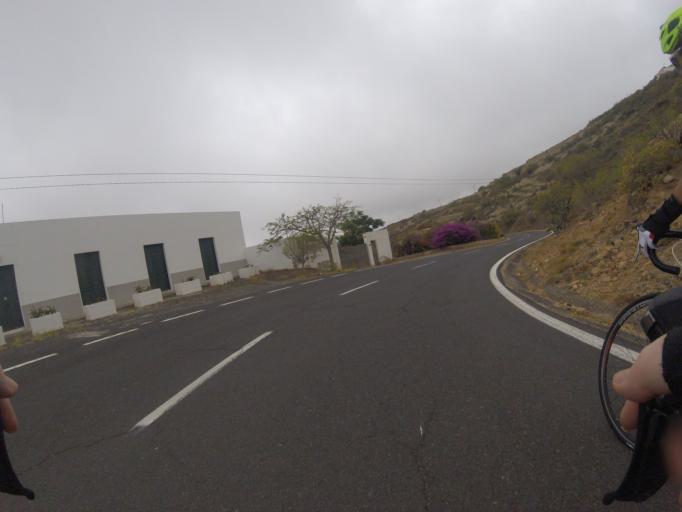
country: ES
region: Canary Islands
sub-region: Provincia de Santa Cruz de Tenerife
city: Fasnia
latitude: 28.2157
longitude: -16.4521
